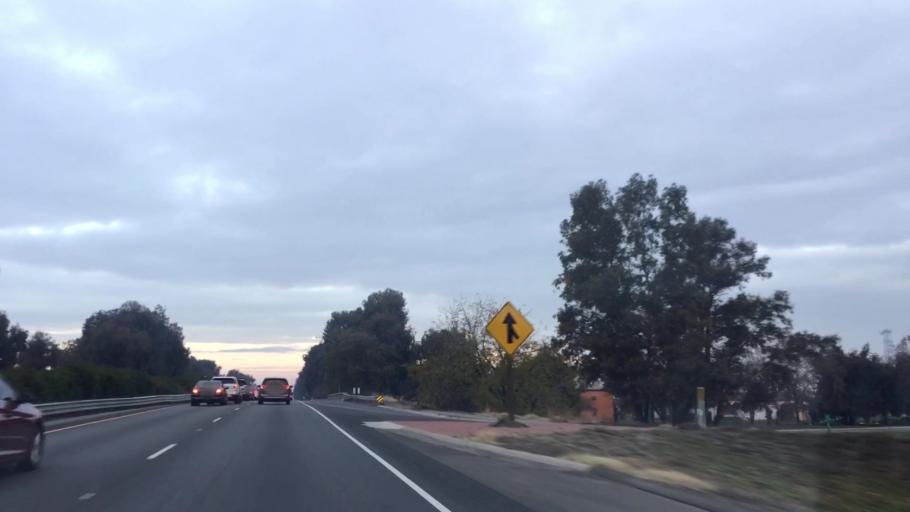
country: US
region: California
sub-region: Yuba County
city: Linda
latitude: 39.1239
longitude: -121.5760
